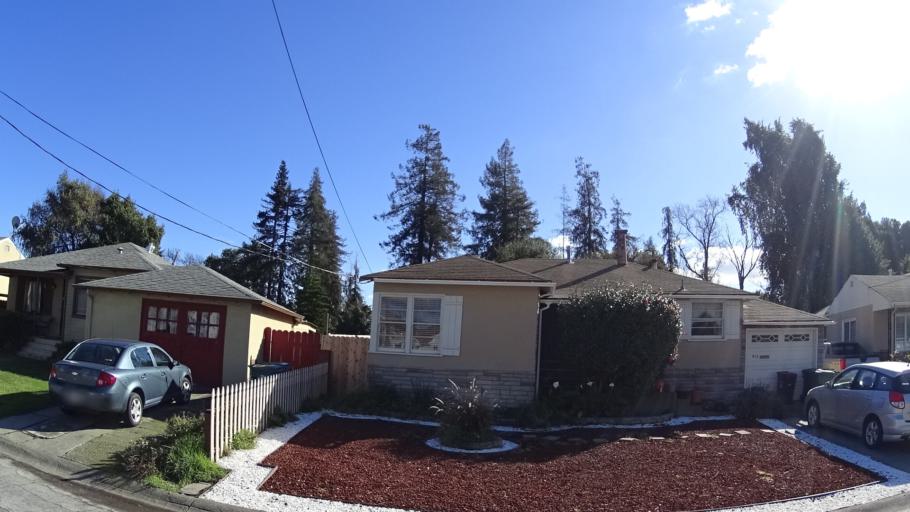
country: US
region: California
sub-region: Alameda County
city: Cherryland
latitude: 37.6862
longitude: -122.1039
